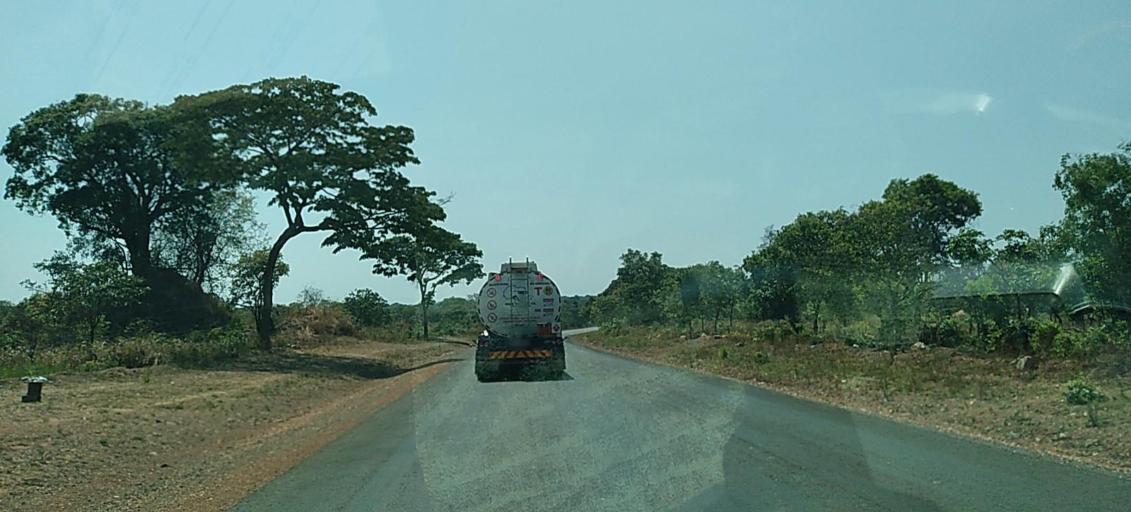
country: ZM
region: North-Western
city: Solwezi
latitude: -12.3621
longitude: 25.9677
